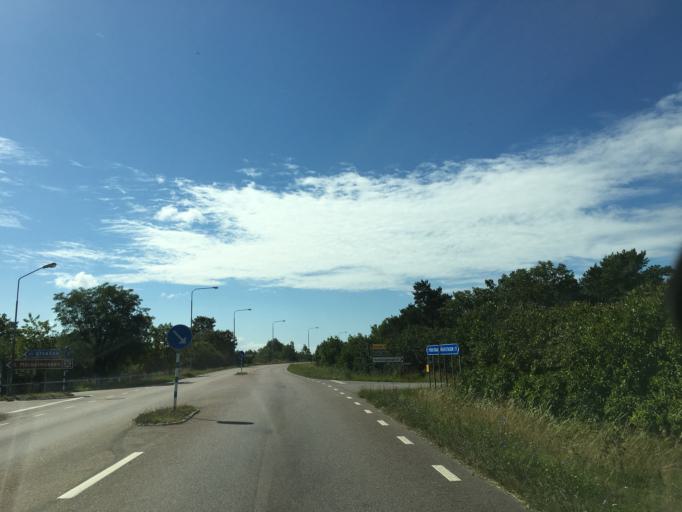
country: SE
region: Kalmar
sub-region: Morbylanga Kommun
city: Moerbylanga
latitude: 56.5386
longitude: 16.4460
